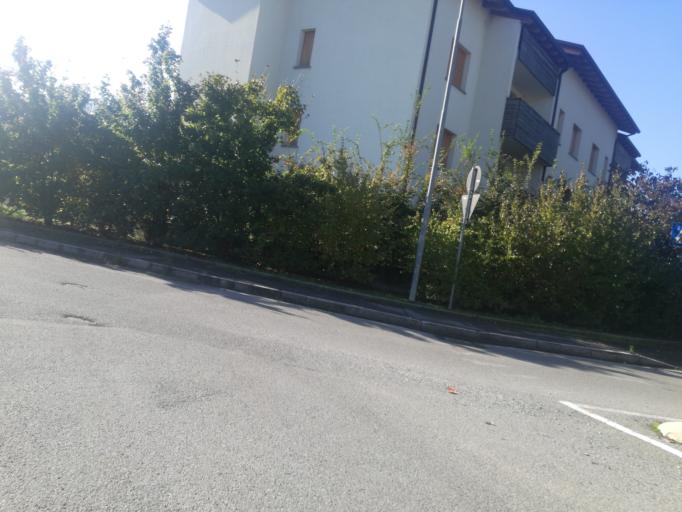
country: IT
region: Lombardy
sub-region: Provincia di Monza e Brianza
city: Porto d'Adda
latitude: 45.6473
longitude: 9.4851
